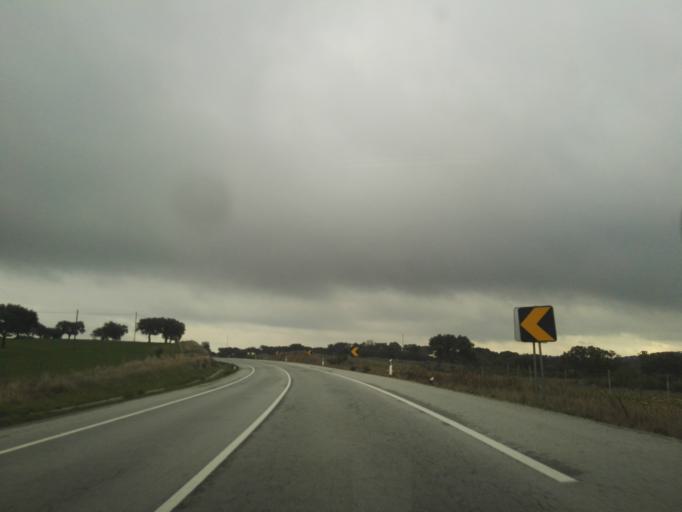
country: PT
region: Portalegre
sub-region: Portalegre
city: Urra
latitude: 39.2113
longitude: -7.3773
